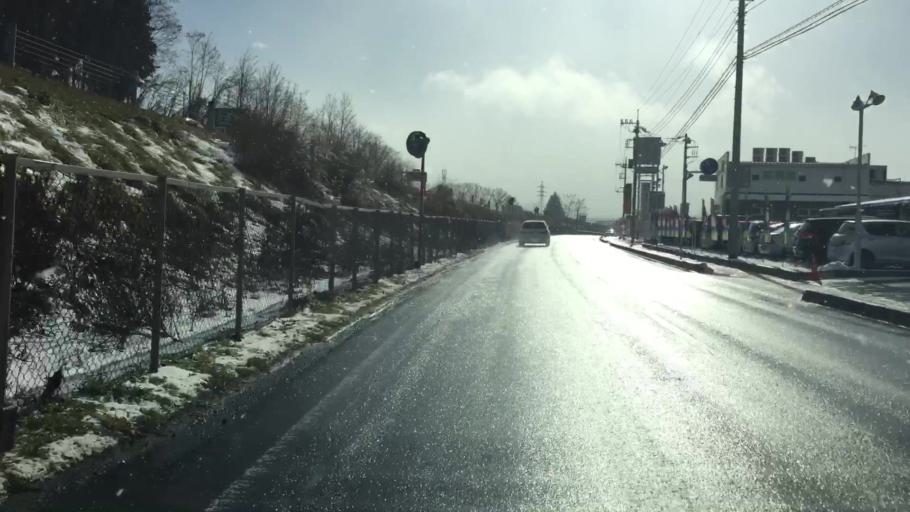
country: JP
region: Gunma
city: Numata
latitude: 36.6643
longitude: 139.0665
